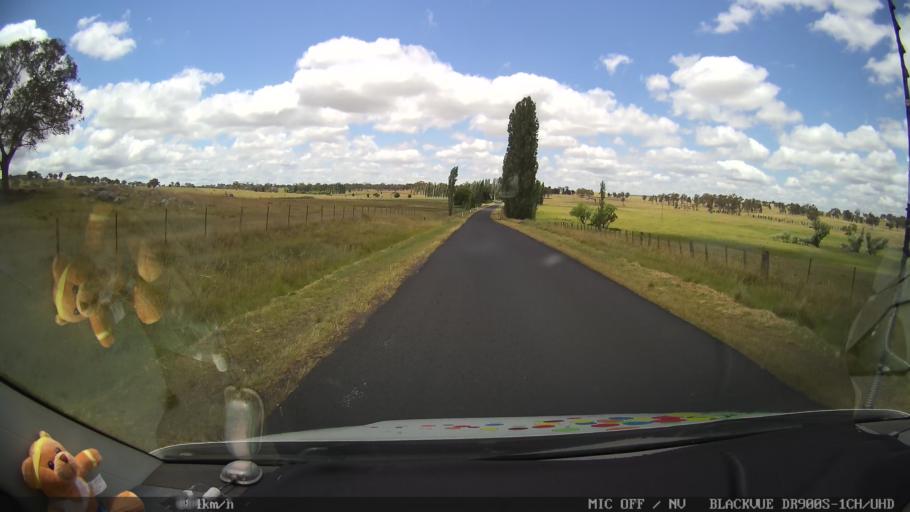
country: AU
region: New South Wales
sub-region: Glen Innes Severn
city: Glen Innes
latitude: -29.4325
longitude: 151.7536
